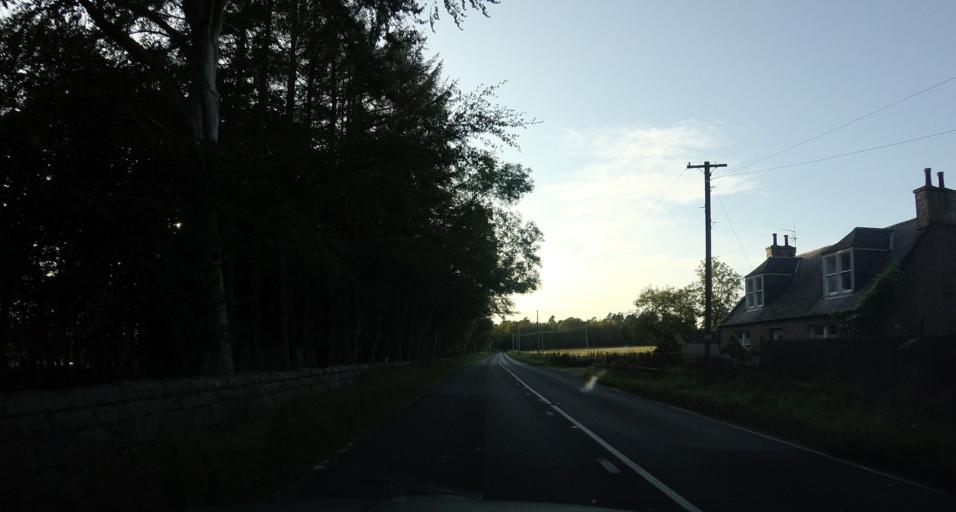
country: GB
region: Scotland
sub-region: Aberdeenshire
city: Kintore
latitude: 57.1634
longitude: -2.3565
